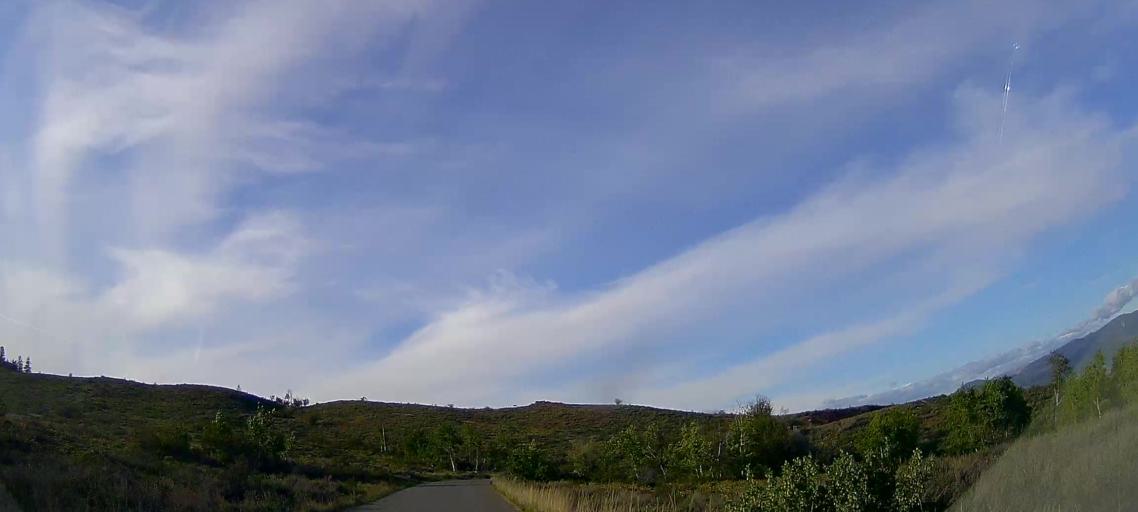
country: US
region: Washington
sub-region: Chelan County
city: Granite Falls
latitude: 48.4696
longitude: -120.2576
